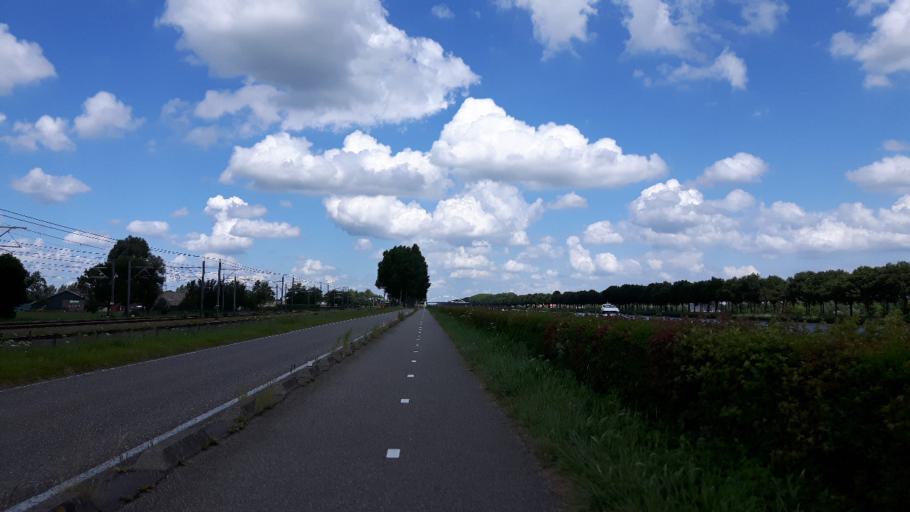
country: NL
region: Utrecht
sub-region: Stichtse Vecht
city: Vreeland
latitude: 52.2109
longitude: 5.0022
